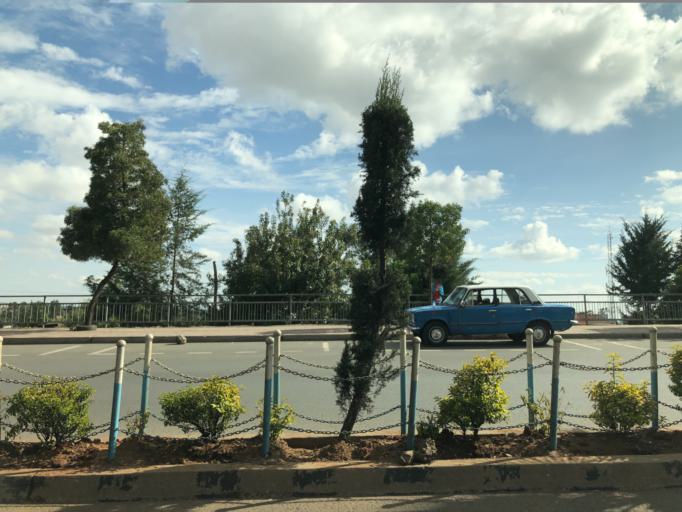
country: ET
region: Adis Abeba
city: Addis Ababa
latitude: 9.0316
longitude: 38.7716
